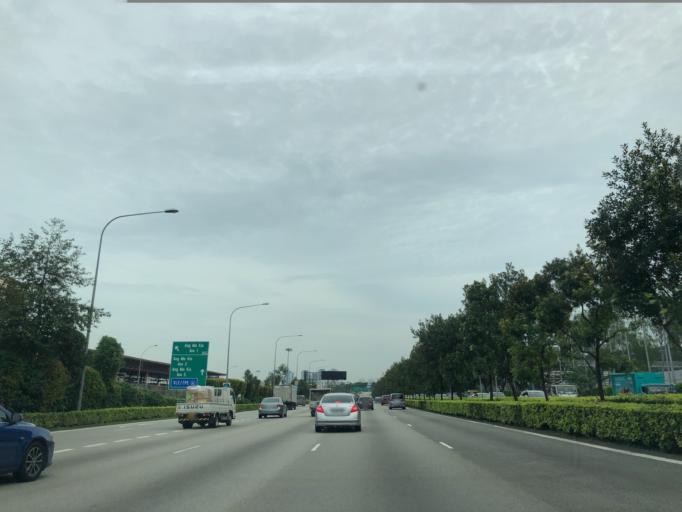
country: SG
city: Singapore
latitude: 1.3469
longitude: 103.8591
